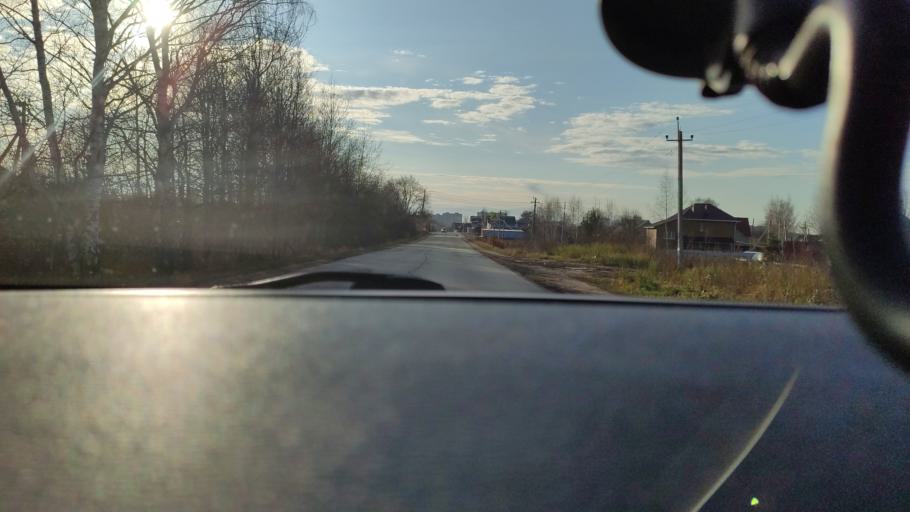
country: RU
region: Perm
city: Kondratovo
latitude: 58.0562
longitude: 56.0278
